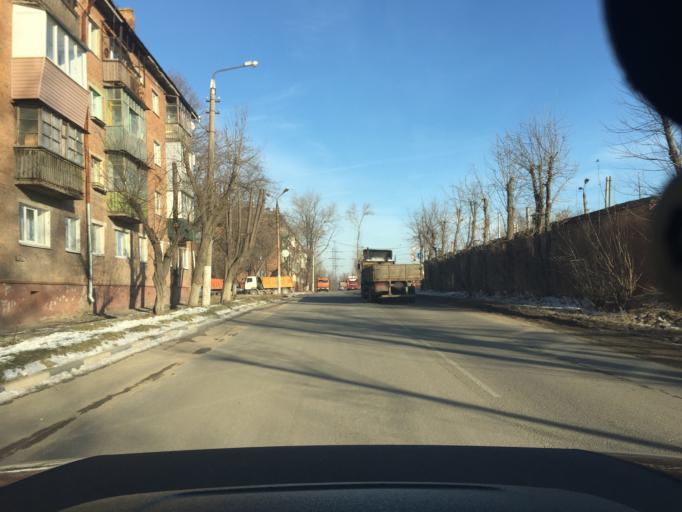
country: RU
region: Tula
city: Tula
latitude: 54.1774
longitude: 37.7090
